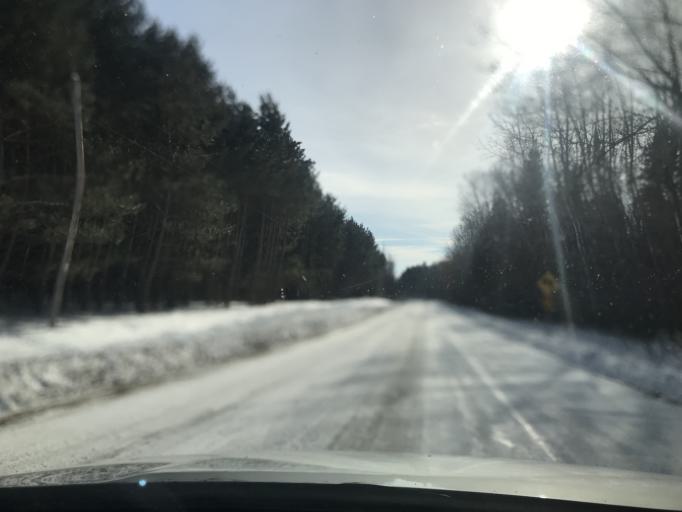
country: US
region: Wisconsin
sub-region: Oconto County
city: Gillett
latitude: 45.1231
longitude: -88.2499
